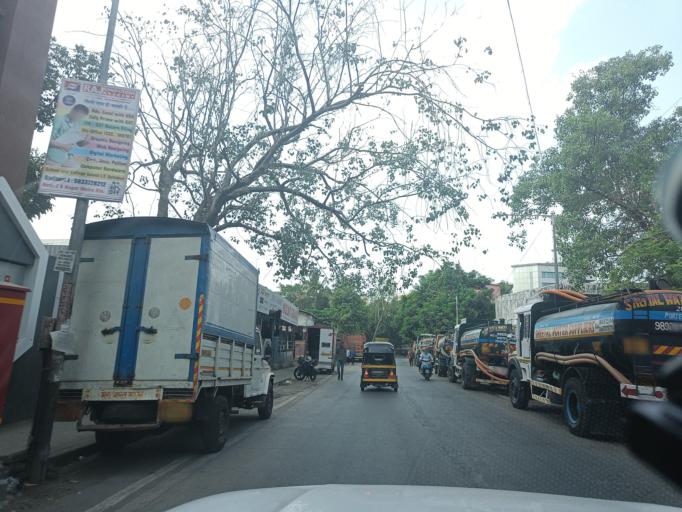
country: IN
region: Maharashtra
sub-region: Mumbai Suburban
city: Powai
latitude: 19.1157
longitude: 72.8683
